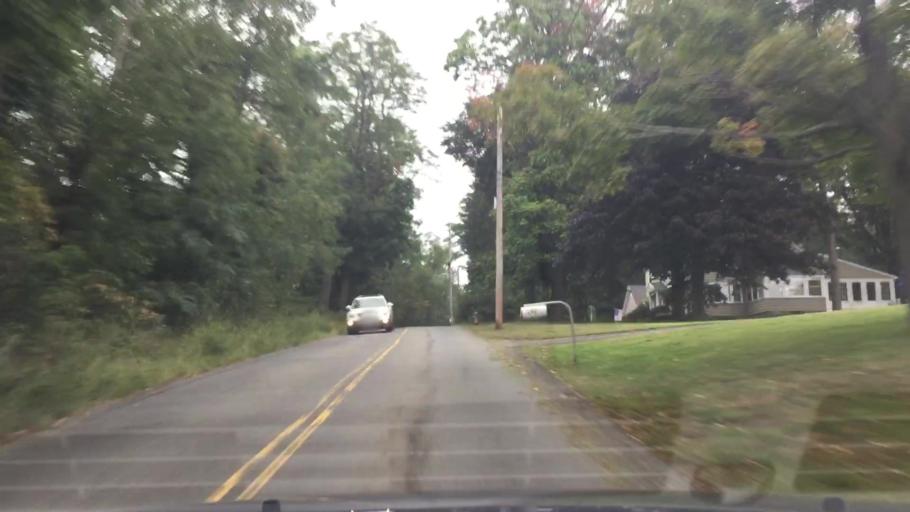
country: US
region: Massachusetts
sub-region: Essex County
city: North Andover
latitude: 42.7259
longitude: -71.0992
